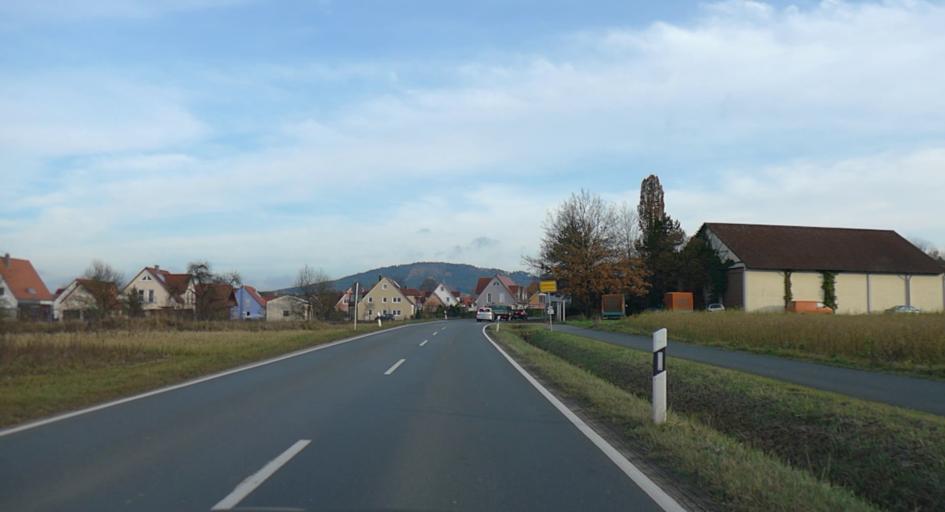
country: DE
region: Bavaria
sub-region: Upper Franconia
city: Poxdorf
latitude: 49.6626
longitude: 11.0818
